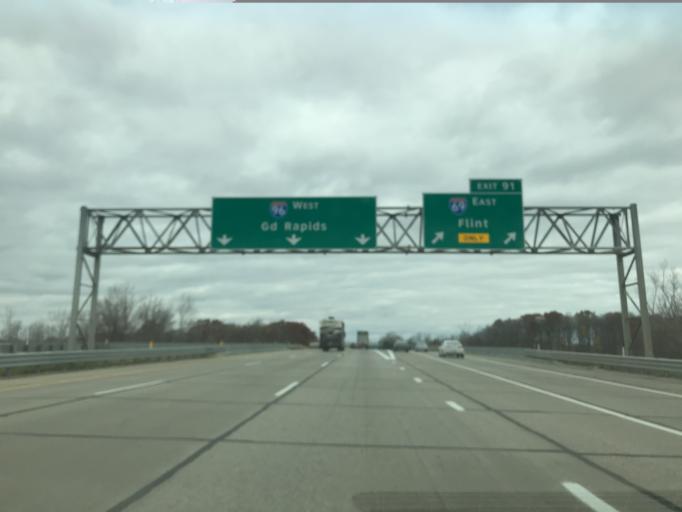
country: US
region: Michigan
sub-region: Eaton County
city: Waverly
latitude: 42.7732
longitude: -84.6692
